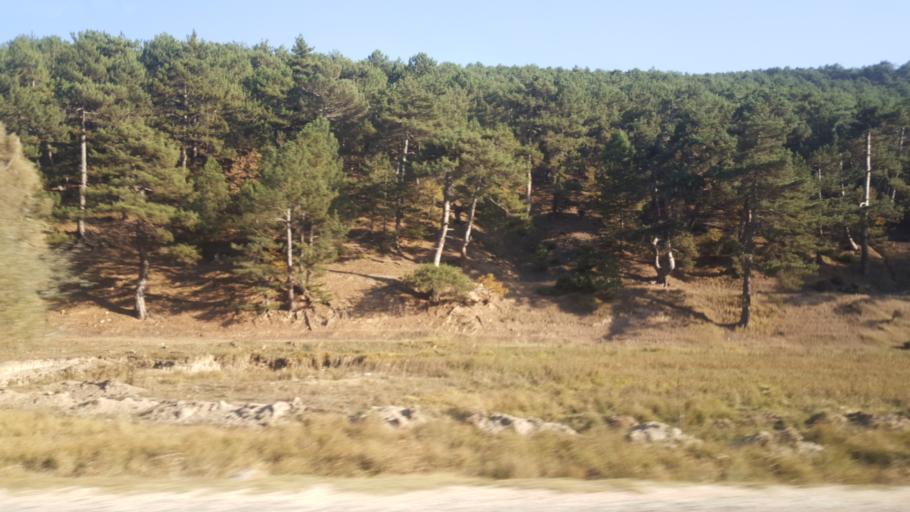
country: TR
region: Eskisehir
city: Kirka
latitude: 39.1072
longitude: 30.5825
